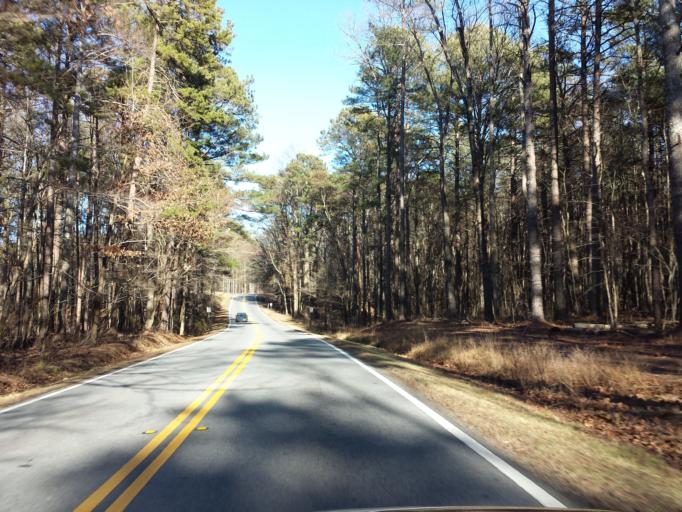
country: US
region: Georgia
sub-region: Cobb County
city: Marietta
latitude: 33.9824
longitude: -84.5845
